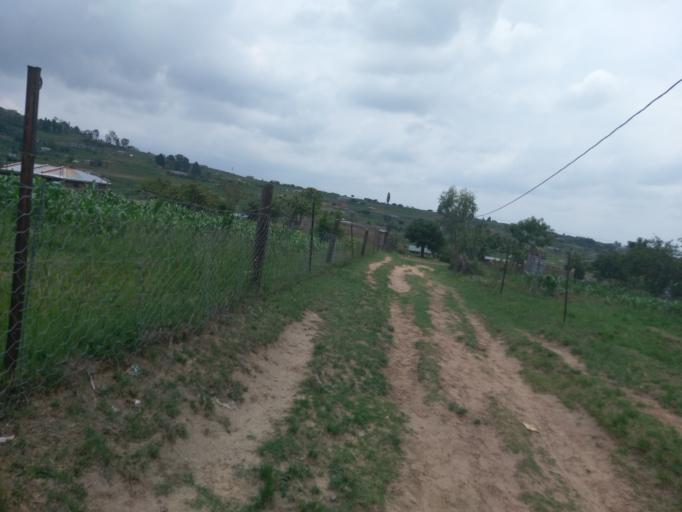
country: LS
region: Leribe
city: Leribe
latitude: -29.0294
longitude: 28.0241
